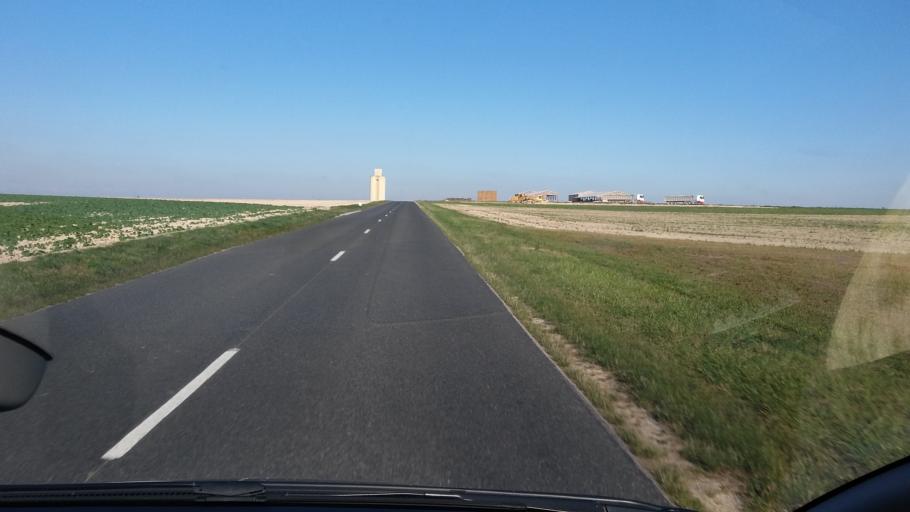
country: FR
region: Champagne-Ardenne
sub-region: Departement de la Marne
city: Connantre
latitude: 48.7951
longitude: 3.8983
